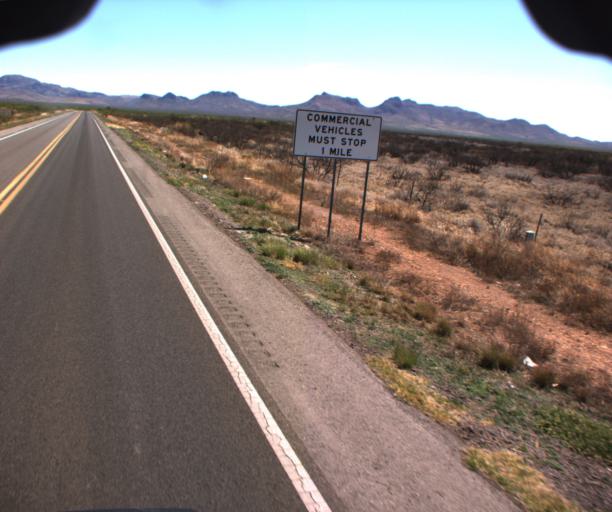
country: US
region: Arizona
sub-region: Cochise County
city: Douglas
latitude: 31.3730
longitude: -109.5274
